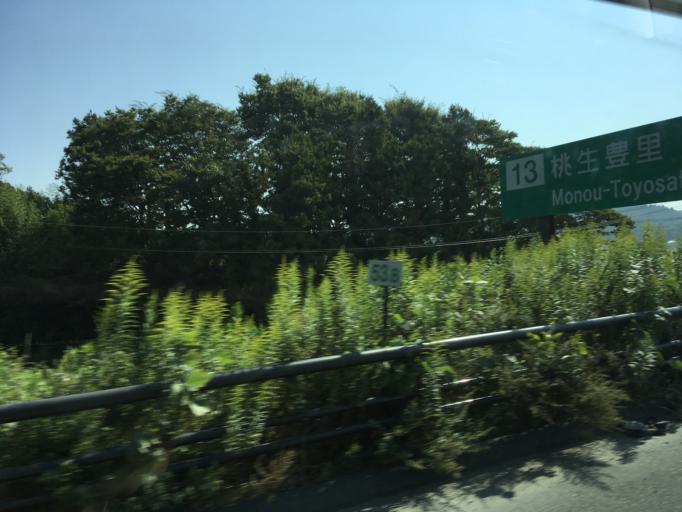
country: JP
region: Miyagi
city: Wakuya
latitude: 38.5794
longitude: 141.2741
